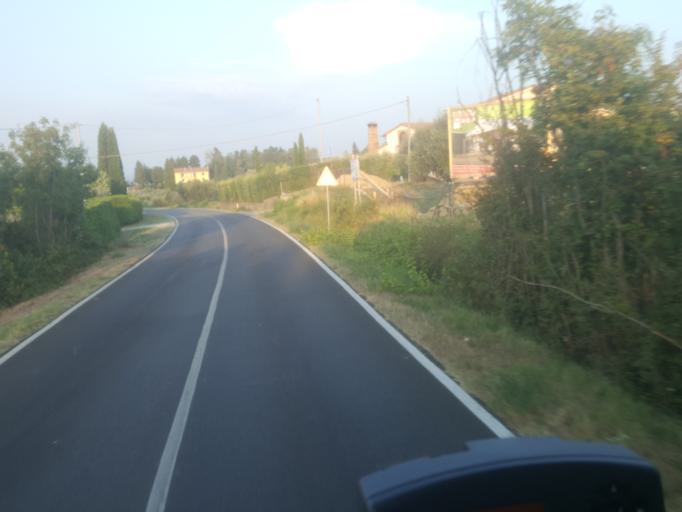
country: IT
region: Tuscany
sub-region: Province of Florence
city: Gambassi Terme
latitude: 43.5442
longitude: 10.9678
